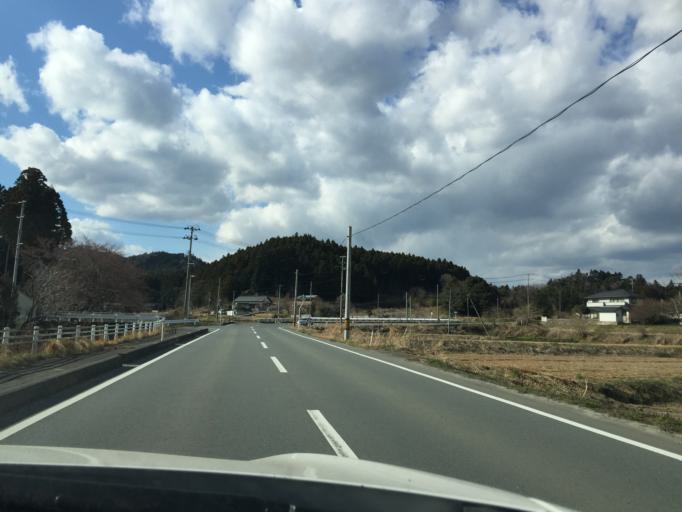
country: JP
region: Fukushima
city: Namie
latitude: 37.2778
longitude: 140.9764
